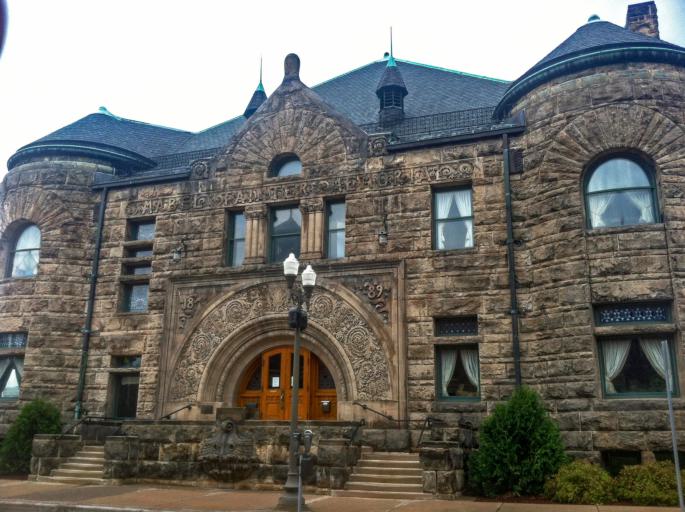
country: US
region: Wisconsin
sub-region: Dunn County
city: Menomonie
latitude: 44.8765
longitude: -91.9279
